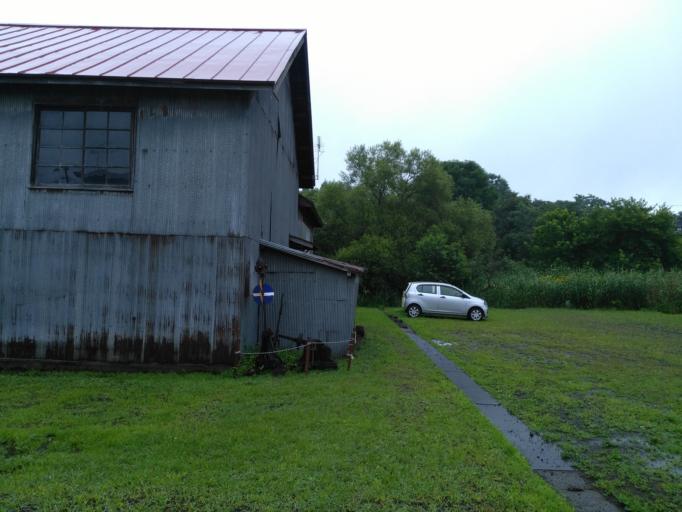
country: JP
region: Aomori
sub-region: Misawa Shi
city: Inuotose
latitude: 40.6965
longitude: 141.1651
